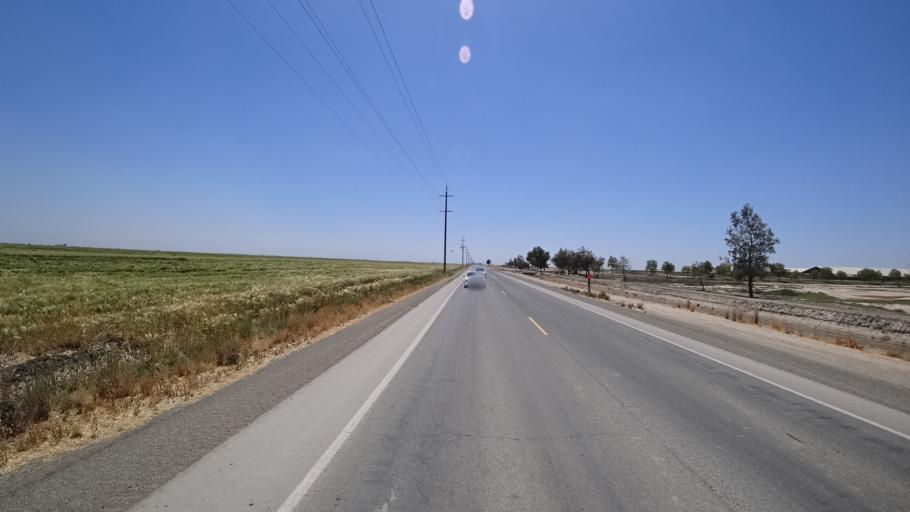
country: US
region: California
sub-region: Kings County
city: Home Garden
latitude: 36.1905
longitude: -119.6459
